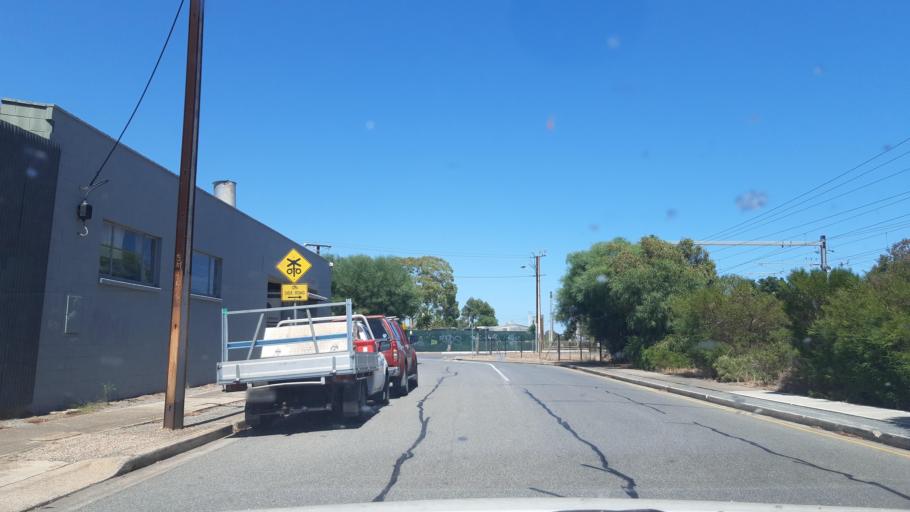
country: AU
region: South Australia
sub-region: Mitcham
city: Clarence Gardens
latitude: -34.9792
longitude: 138.5695
